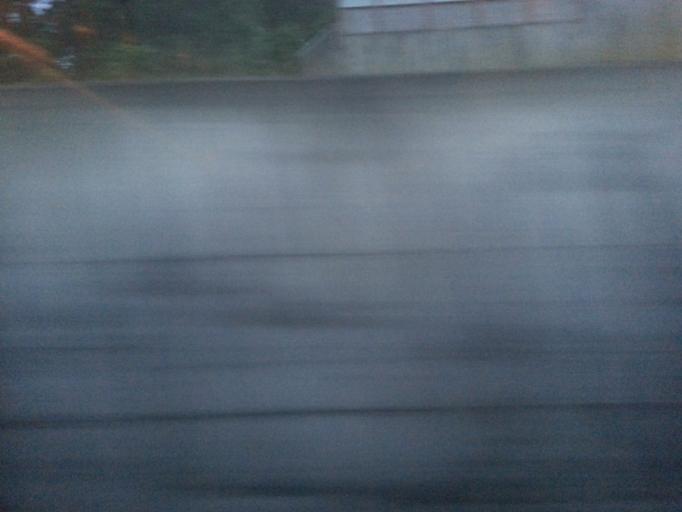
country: NO
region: Akershus
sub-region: Skedsmo
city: Lillestrom
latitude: 59.9525
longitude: 11.0267
